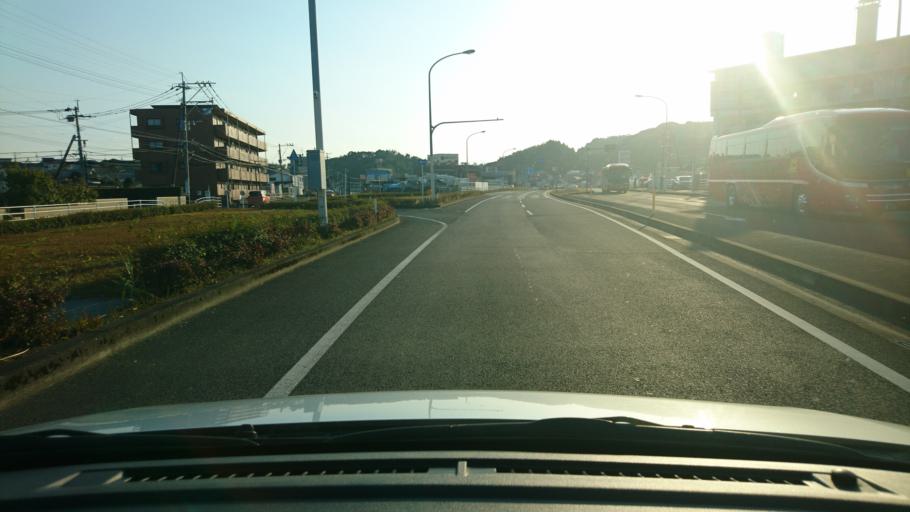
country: JP
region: Miyazaki
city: Miyazaki-shi
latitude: 31.9754
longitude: 131.4420
